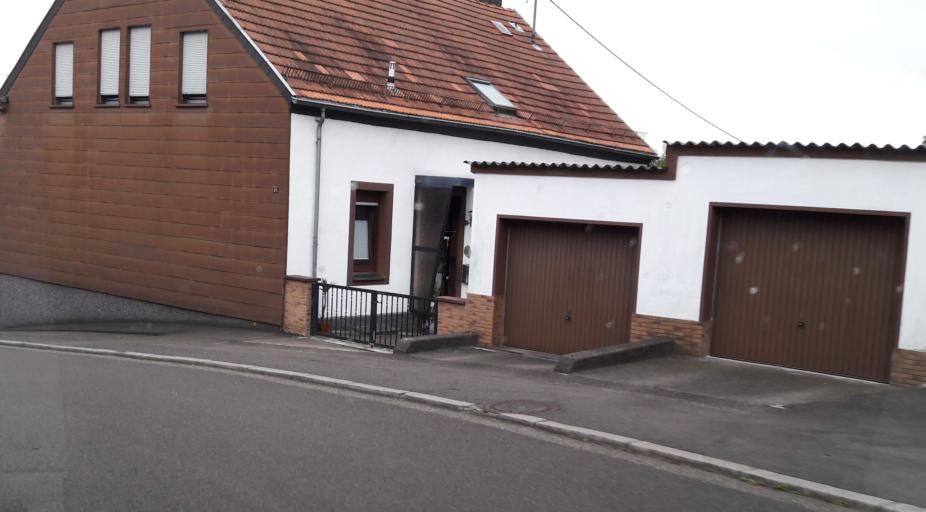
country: DE
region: Saarland
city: Spiesen-Elversberg
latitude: 49.3174
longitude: 7.1472
